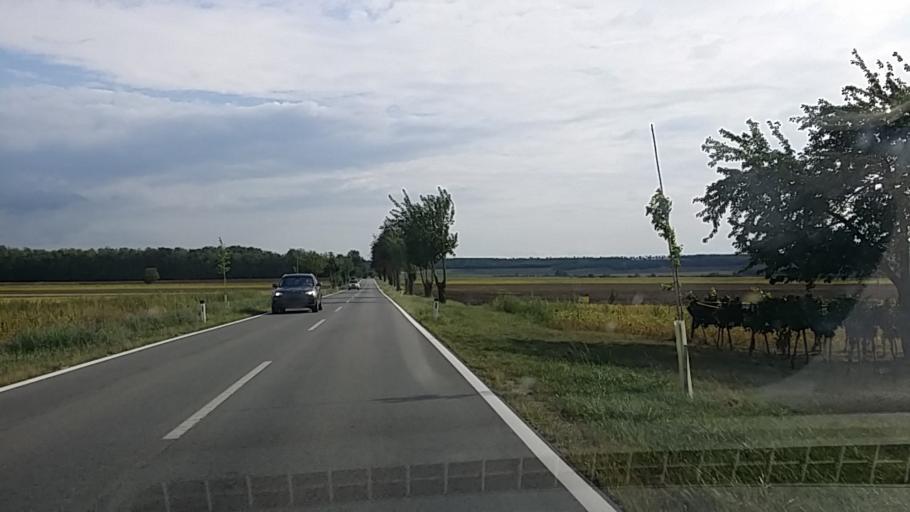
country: AT
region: Burgenland
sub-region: Eisenstadt-Umgebung
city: Sankt Margarethen im Burgenland
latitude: 47.7933
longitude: 16.6182
